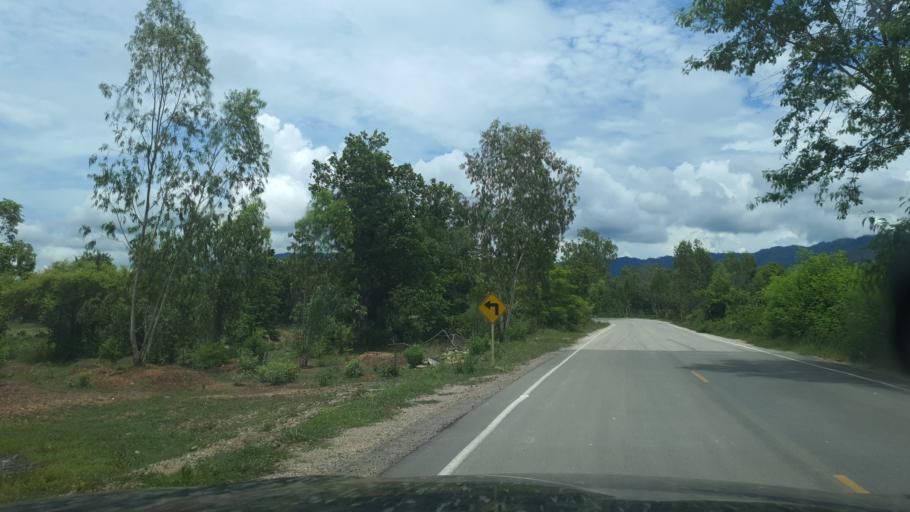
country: TH
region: Lampang
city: Sop Prap
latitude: 17.9138
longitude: 99.3960
